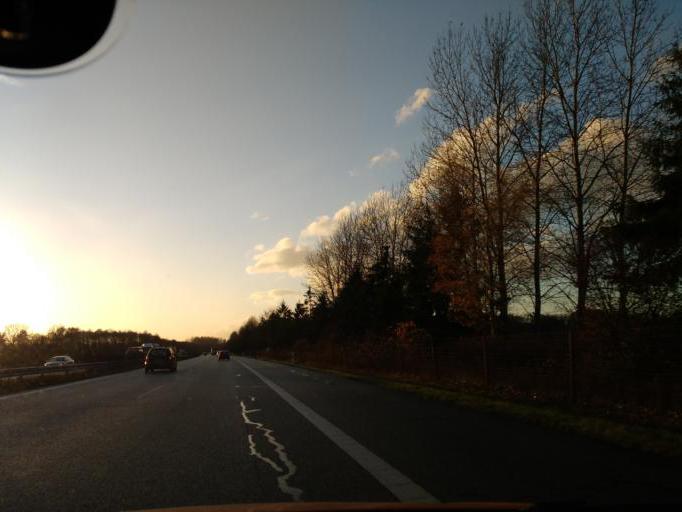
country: DE
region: Mecklenburg-Vorpommern
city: Hagenow
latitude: 53.4876
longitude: 11.2343
